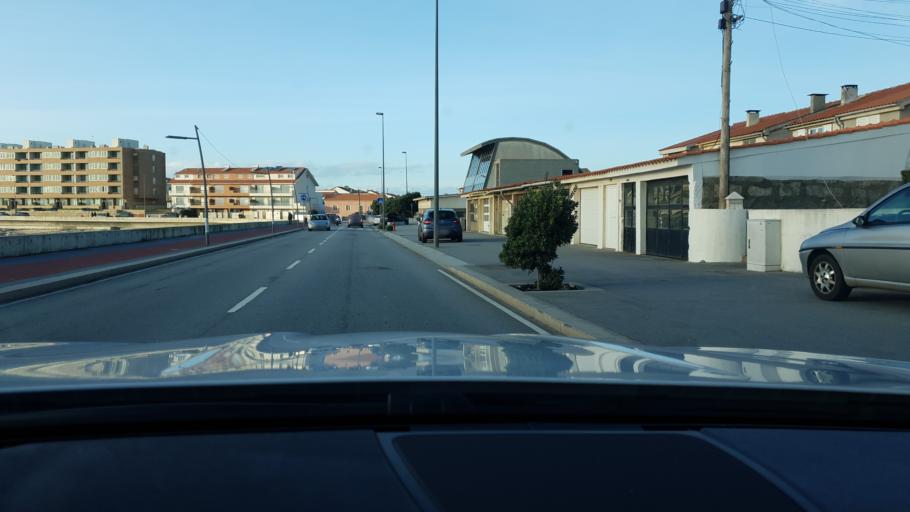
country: PT
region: Porto
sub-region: Matosinhos
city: Santa Cruz do Bispo
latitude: 41.2253
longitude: -8.7163
